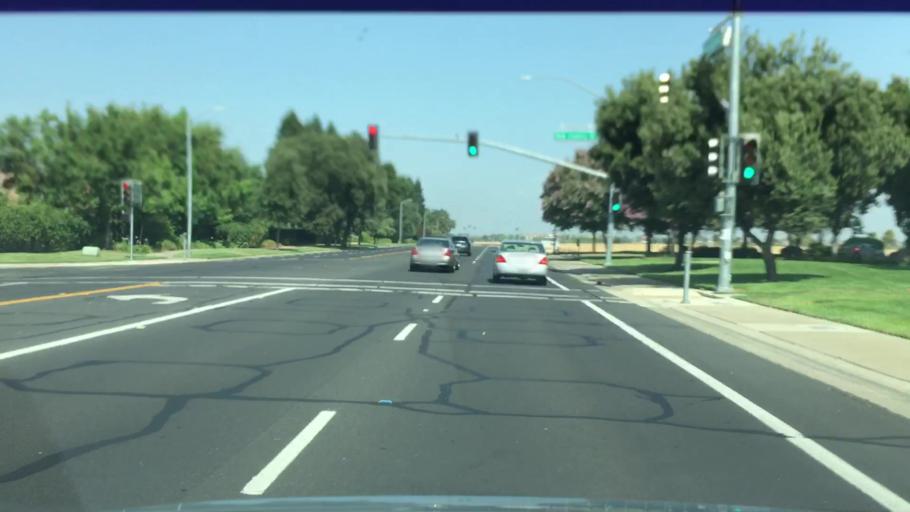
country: US
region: California
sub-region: Sacramento County
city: Laguna
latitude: 38.4266
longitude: -121.4092
